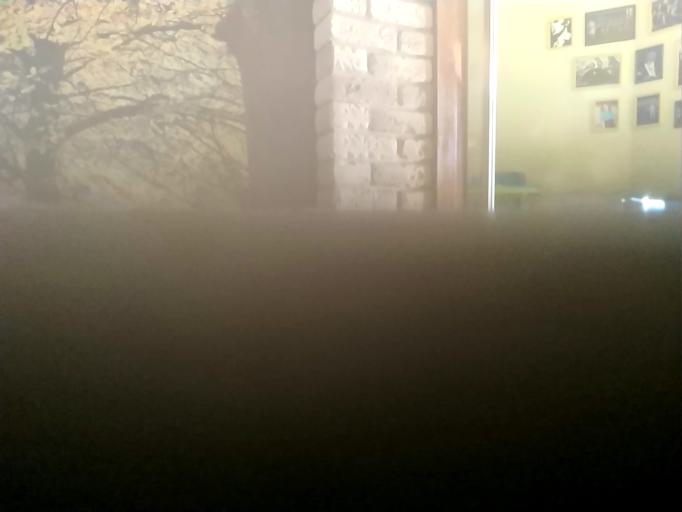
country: RU
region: Smolensk
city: Temkino
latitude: 54.8588
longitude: 34.9913
